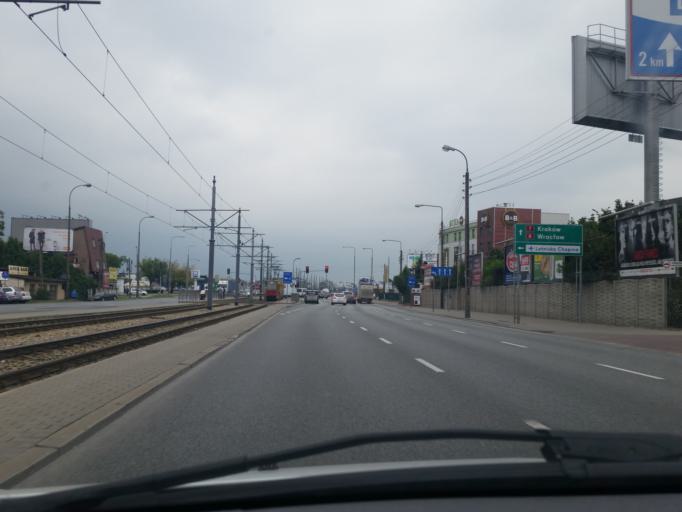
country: PL
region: Masovian Voivodeship
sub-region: Warszawa
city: Wlochy
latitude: 52.1873
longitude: 20.9554
